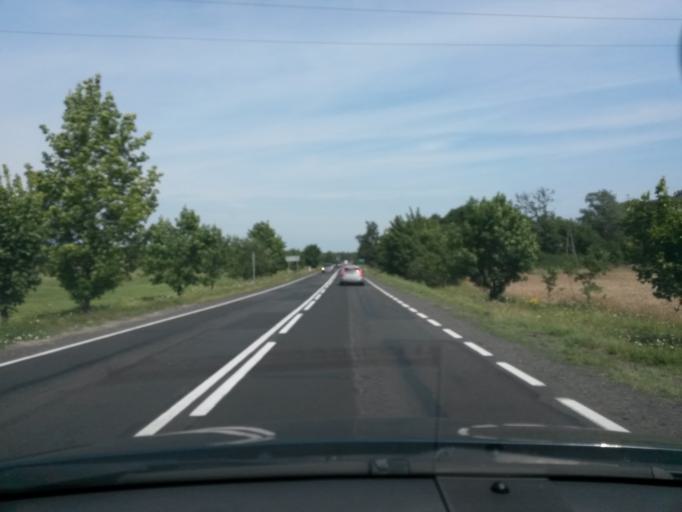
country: PL
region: Lower Silesian Voivodeship
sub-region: Powiat legnicki
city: Prochowice
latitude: 51.2833
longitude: 16.3476
